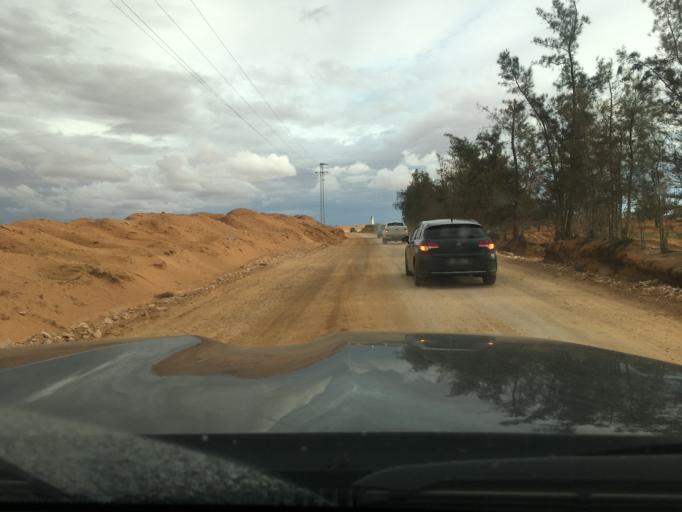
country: TN
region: Madanin
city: Medenine
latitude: 33.2736
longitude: 10.5643
